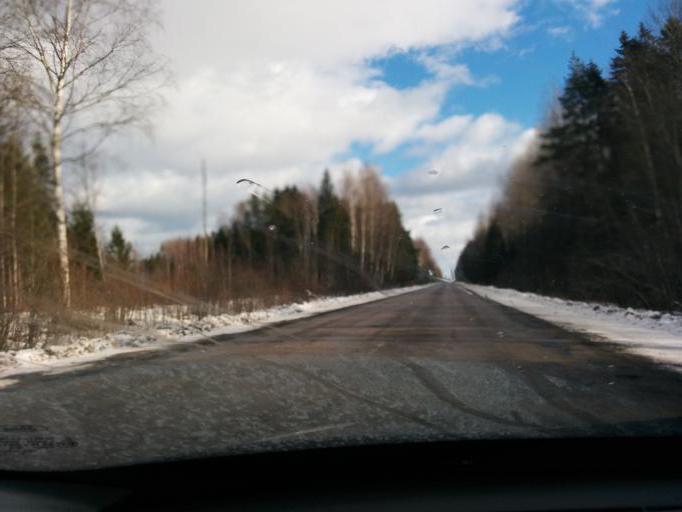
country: LV
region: Cesvaine
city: Cesvaine
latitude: 57.2364
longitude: 26.4408
